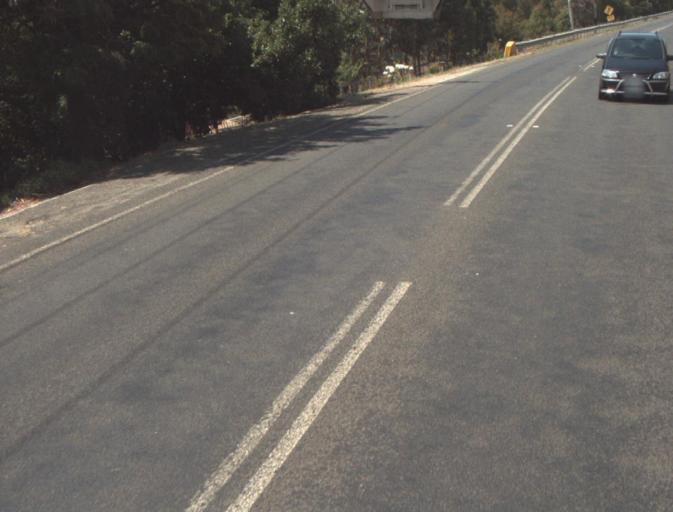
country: AU
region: Tasmania
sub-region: Launceston
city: Summerhill
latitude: -41.4952
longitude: 147.1717
